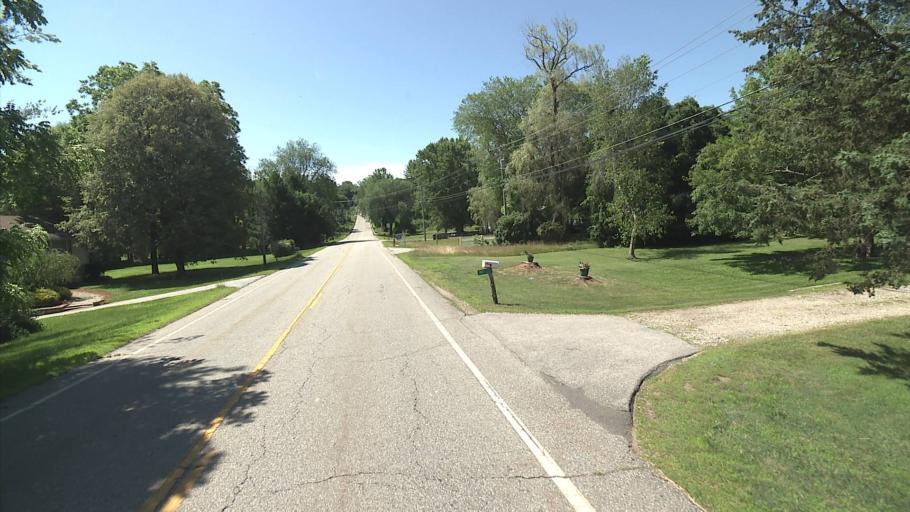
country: US
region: Connecticut
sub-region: Windham County
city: Willimantic
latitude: 41.6568
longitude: -72.2275
